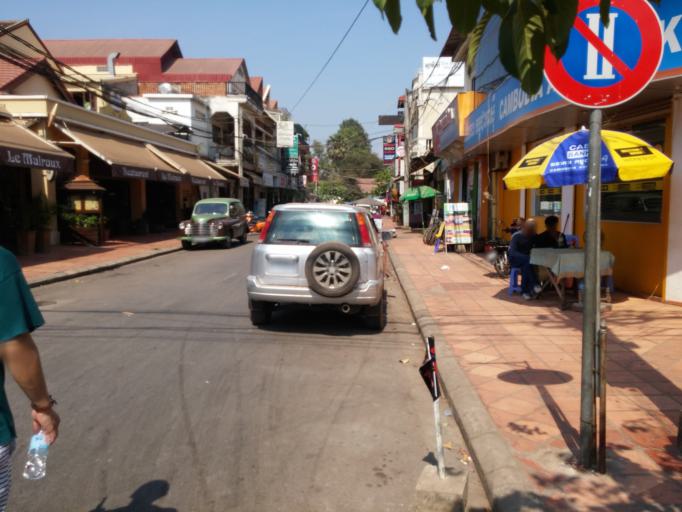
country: KH
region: Siem Reap
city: Siem Reap
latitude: 13.3553
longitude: 103.8539
